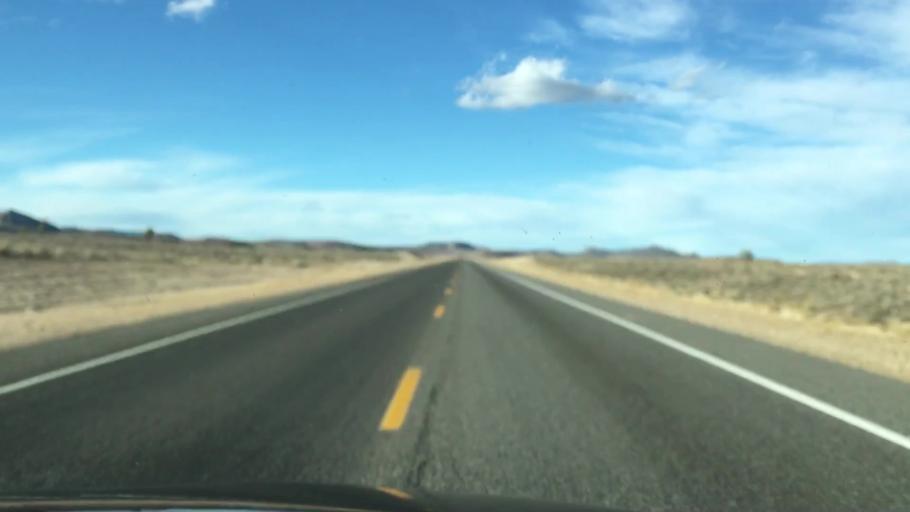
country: US
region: Nevada
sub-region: Esmeralda County
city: Goldfield
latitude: 37.5857
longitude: -117.2070
